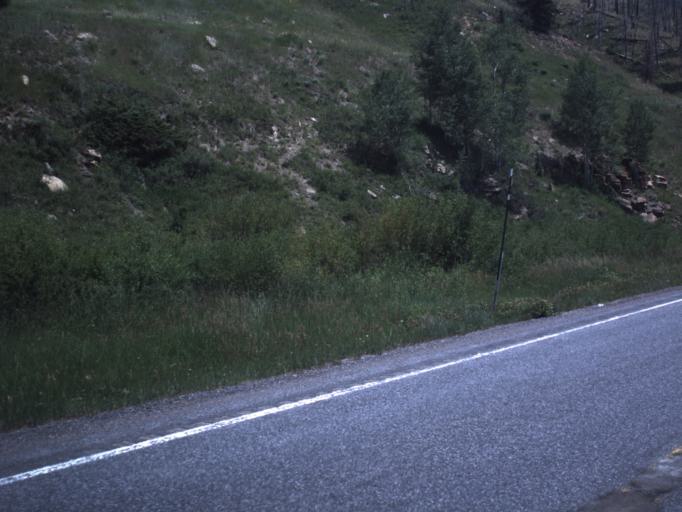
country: US
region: Utah
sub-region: Sanpete County
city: Fairview
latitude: 39.5766
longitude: -111.1843
